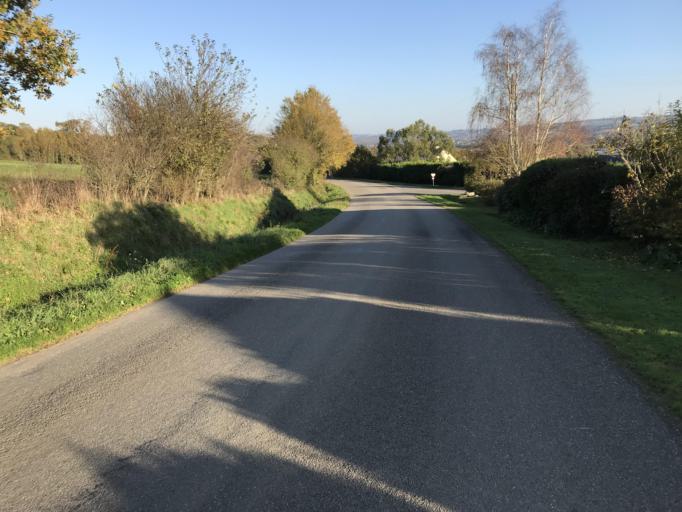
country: FR
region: Brittany
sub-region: Departement du Finistere
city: Hopital-Camfrout
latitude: 48.2995
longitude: -4.2190
